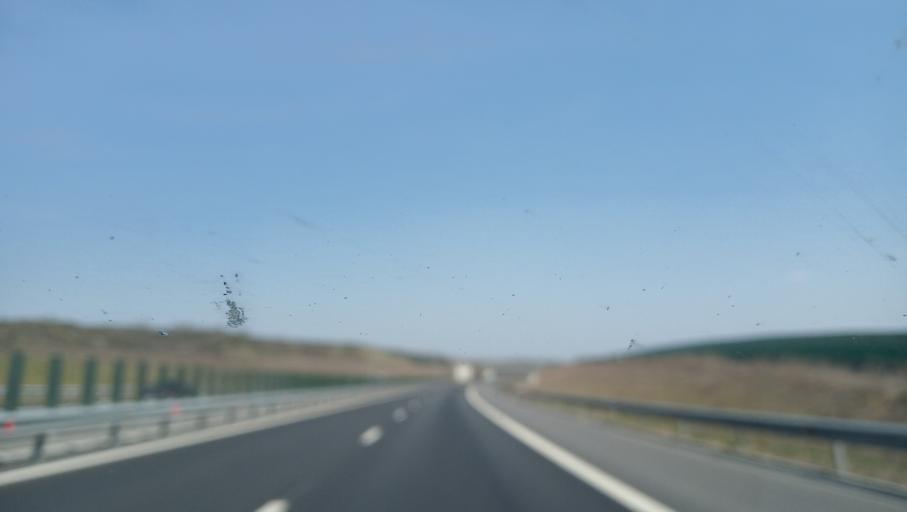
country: RO
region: Alba
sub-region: Comuna Miraslau
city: Miraslau
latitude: 46.3829
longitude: 23.7560
